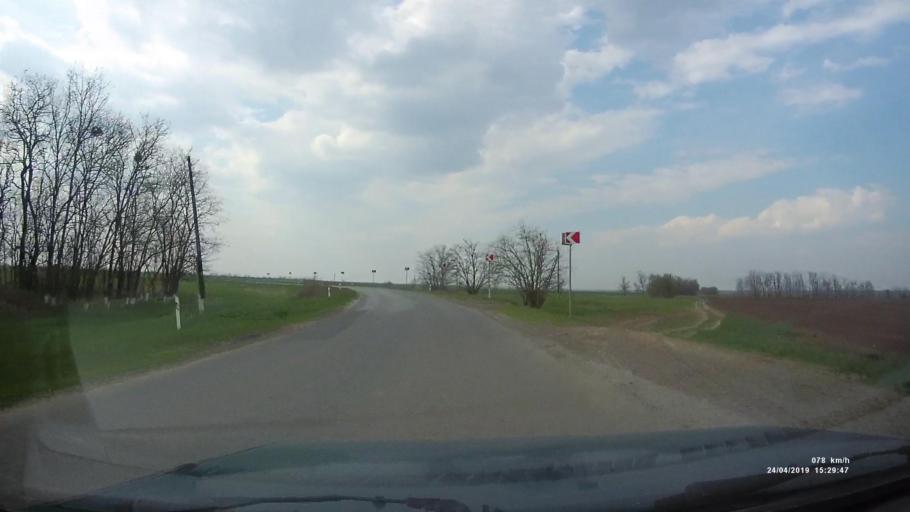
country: RU
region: Rostov
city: Remontnoye
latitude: 46.5983
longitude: 43.0171
